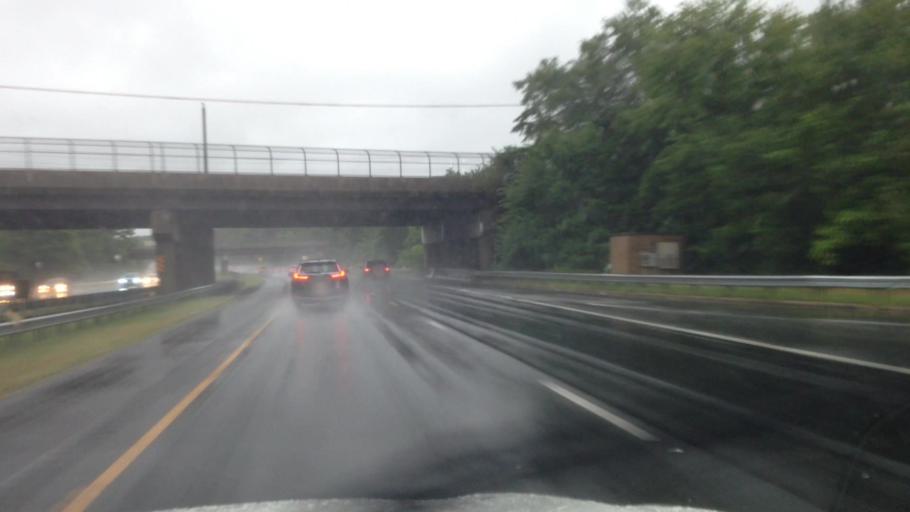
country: US
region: Maryland
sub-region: Prince George's County
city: Landover
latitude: 38.9310
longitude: -76.8970
